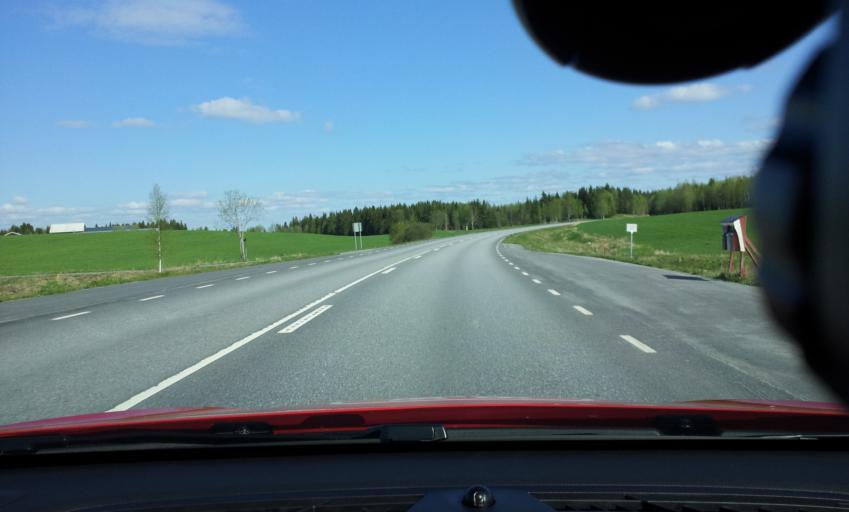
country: SE
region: Jaemtland
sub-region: Krokoms Kommun
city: Krokom
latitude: 63.0761
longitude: 14.2930
